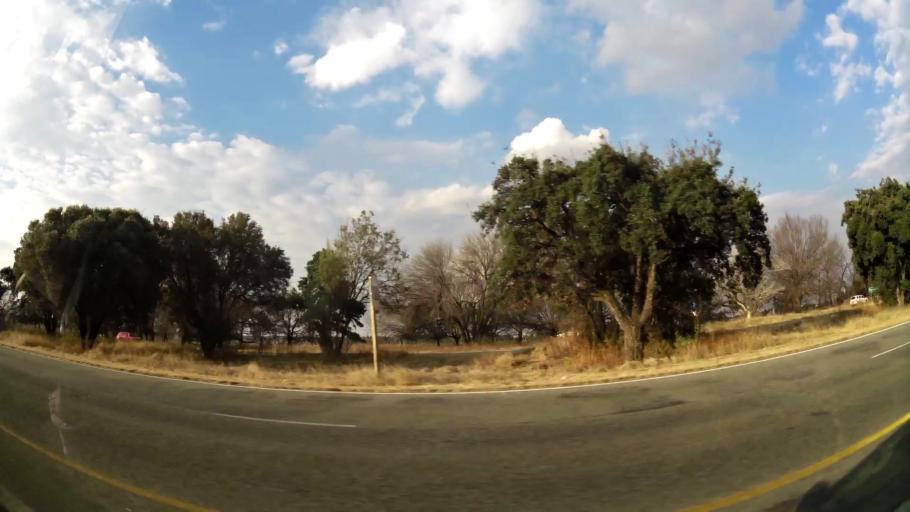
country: ZA
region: Orange Free State
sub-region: Fezile Dabi District Municipality
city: Sasolburg
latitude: -26.7967
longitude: 27.8302
